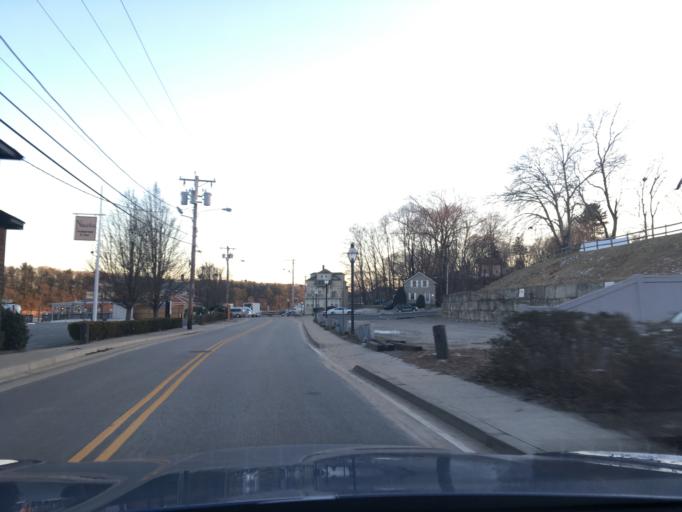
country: US
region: Rhode Island
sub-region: Kent County
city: East Greenwich
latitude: 41.6619
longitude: -71.4456
